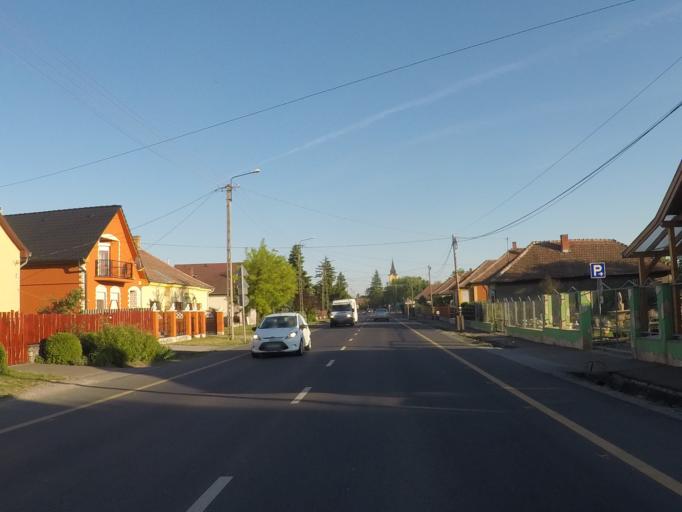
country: HU
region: Heves
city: Fuzesabony
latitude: 47.7231
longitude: 20.4176
